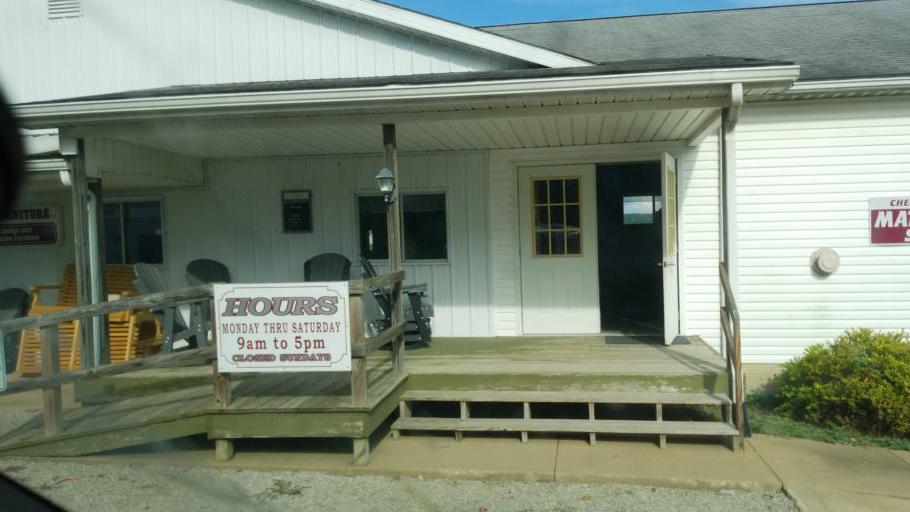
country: US
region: Ohio
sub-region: Knox County
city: Danville
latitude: 40.4643
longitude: -82.2064
